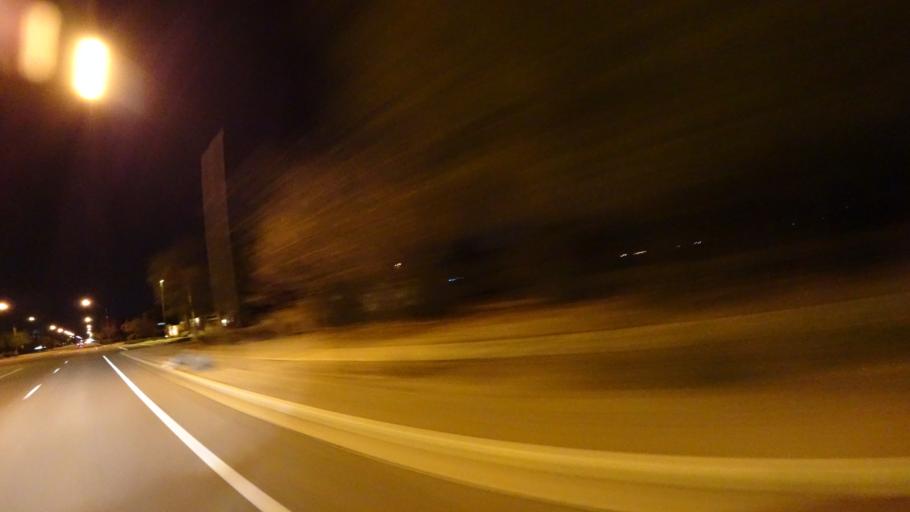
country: US
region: Arizona
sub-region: Maricopa County
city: Gilbert
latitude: 33.3213
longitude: -111.7589
